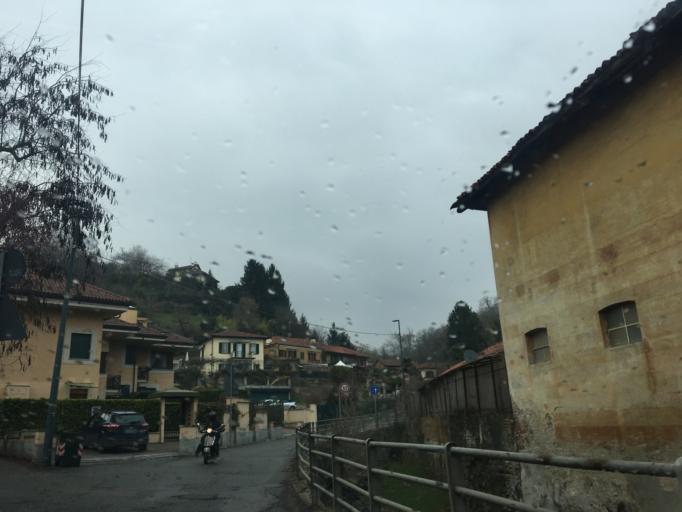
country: IT
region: Piedmont
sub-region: Provincia di Torino
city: Moncalieri
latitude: 45.0199
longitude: 7.6800
